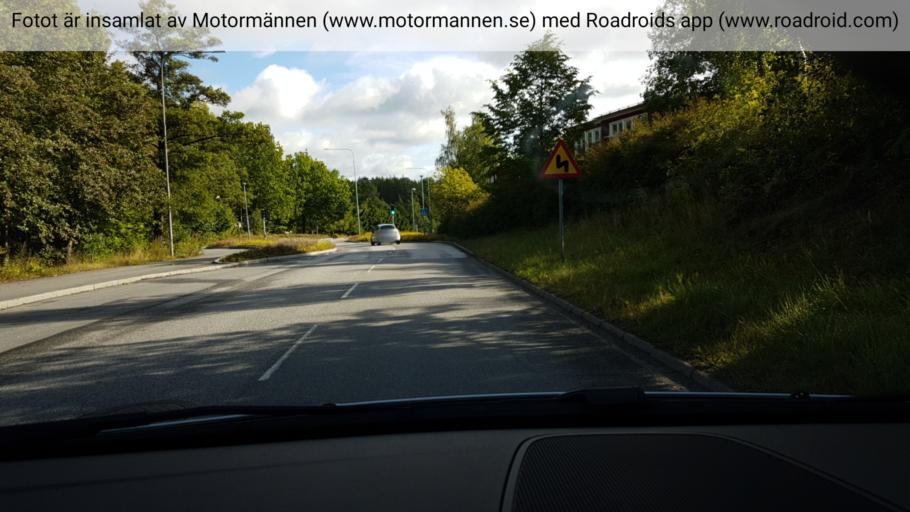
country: SE
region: Stockholm
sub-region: Lidingo
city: Lidingoe
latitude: 59.3828
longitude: 18.1144
